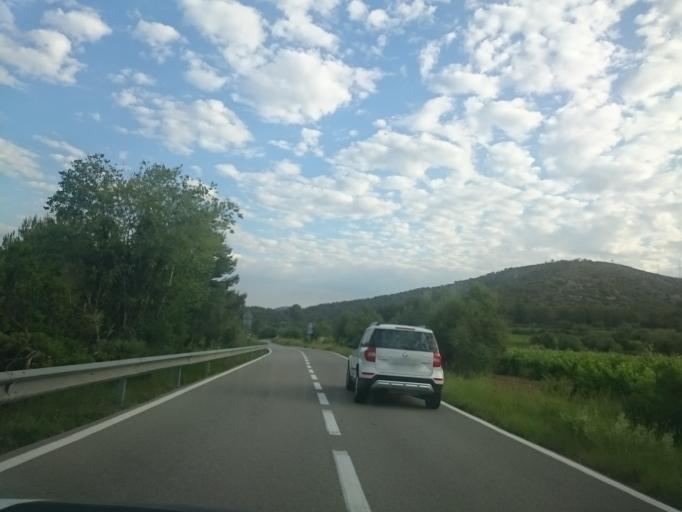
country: ES
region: Catalonia
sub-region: Provincia de Barcelona
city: Cubelles
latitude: 41.2338
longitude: 1.6647
